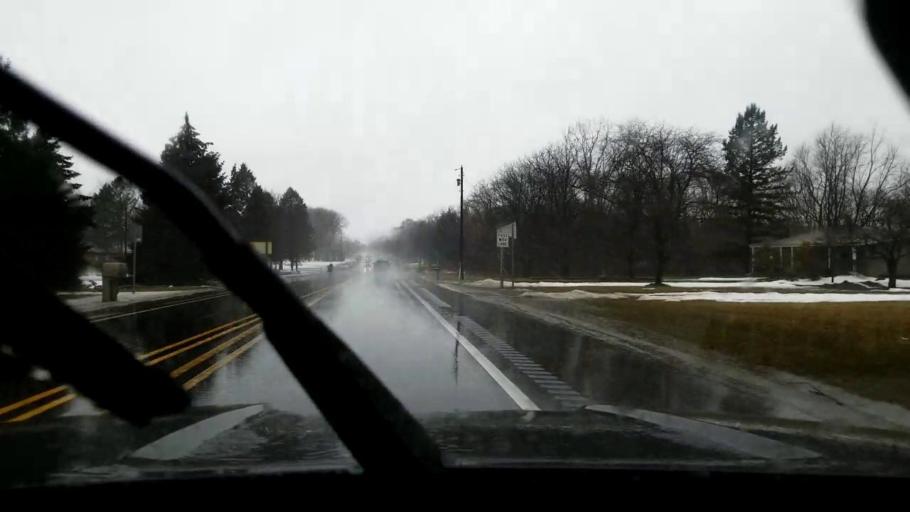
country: US
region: Michigan
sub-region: Jackson County
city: Michigan Center
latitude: 42.1887
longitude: -84.3086
